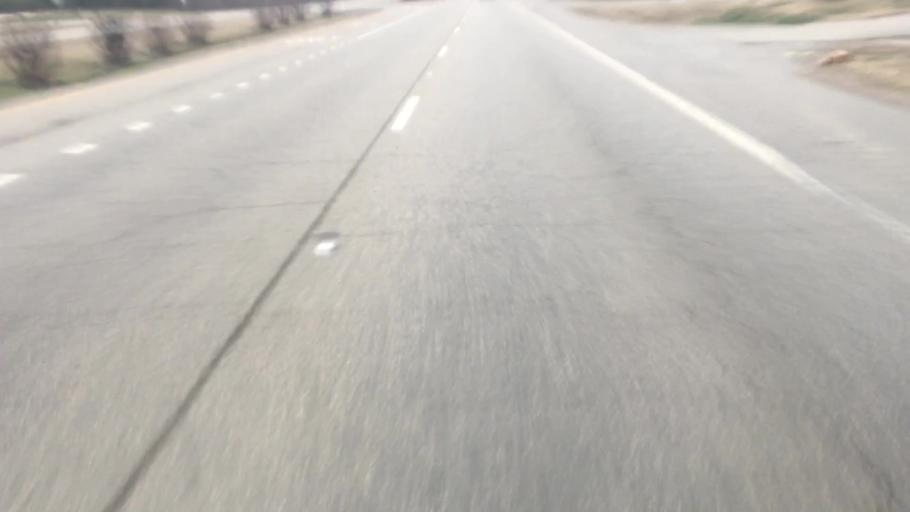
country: US
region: Alabama
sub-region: Walker County
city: Sumiton
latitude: 33.7409
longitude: -87.0366
